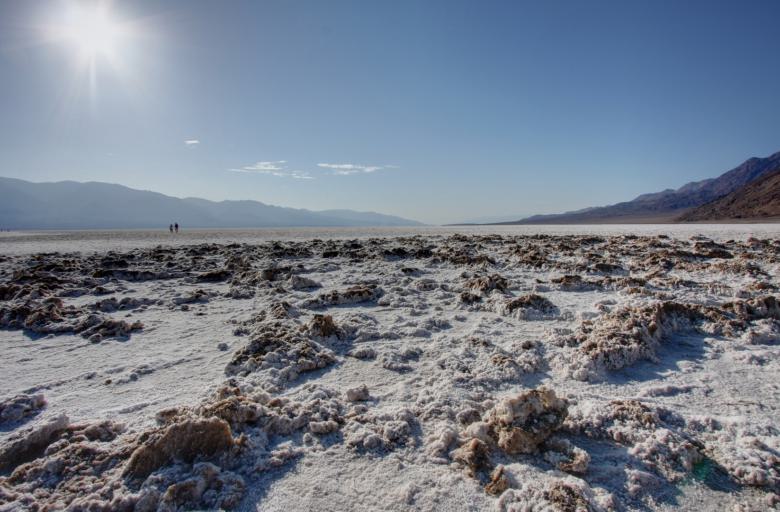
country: US
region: Nevada
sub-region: Nye County
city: Beatty
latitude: 36.2311
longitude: -116.7740
